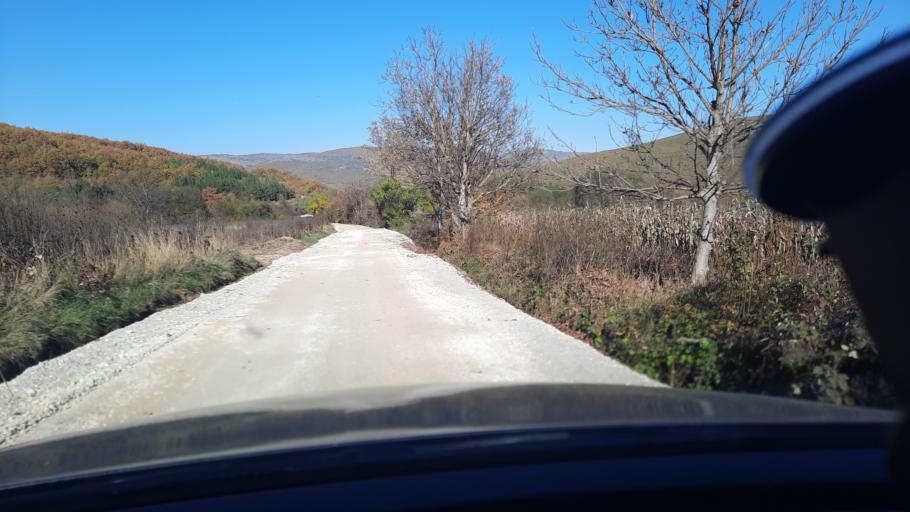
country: MK
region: Demir Hisar
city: Sopotnica
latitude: 41.2705
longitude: 21.0854
